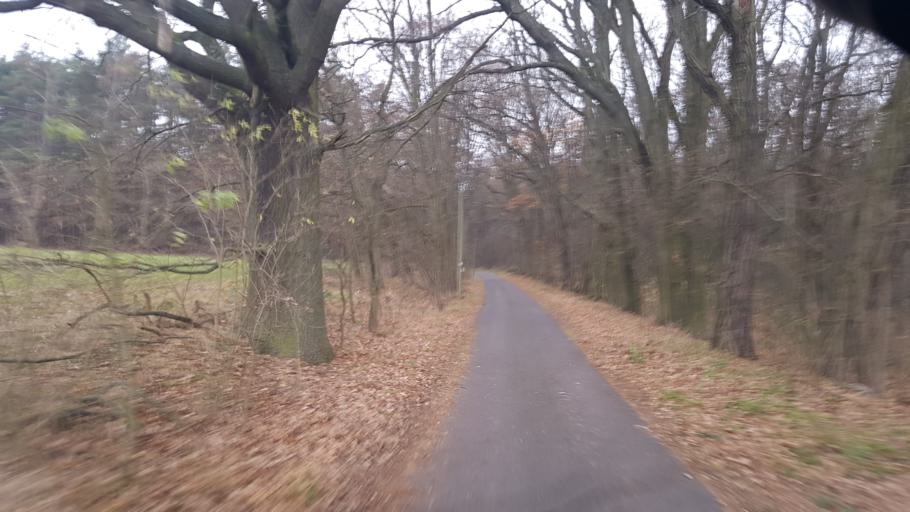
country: DE
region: Brandenburg
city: Schenkendobern
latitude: 51.9676
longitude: 14.6529
